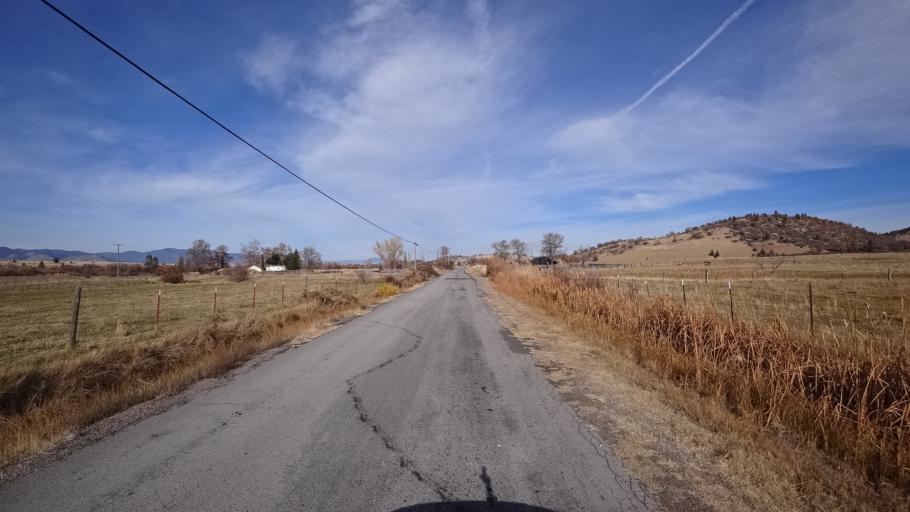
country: US
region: California
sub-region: Siskiyou County
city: Weed
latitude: 41.4633
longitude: -122.4340
